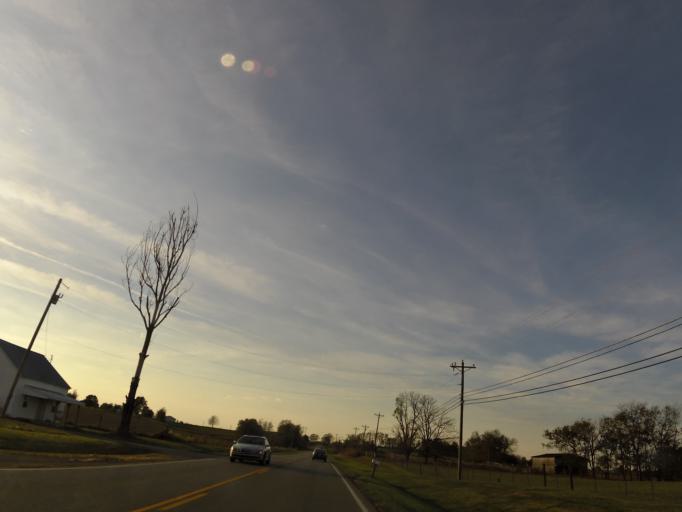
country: US
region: Kentucky
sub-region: Garrard County
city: Lancaster
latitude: 37.6579
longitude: -84.6119
